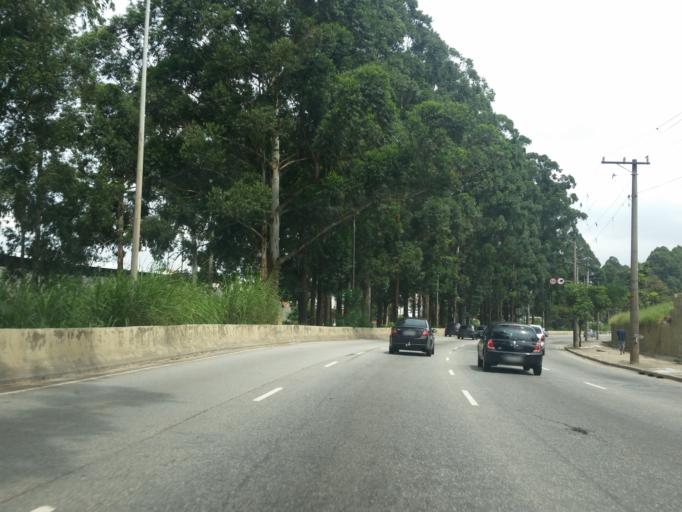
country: BR
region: Sao Paulo
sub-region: Ferraz De Vasconcelos
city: Ferraz de Vasconcelos
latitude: -23.5204
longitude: -46.4559
